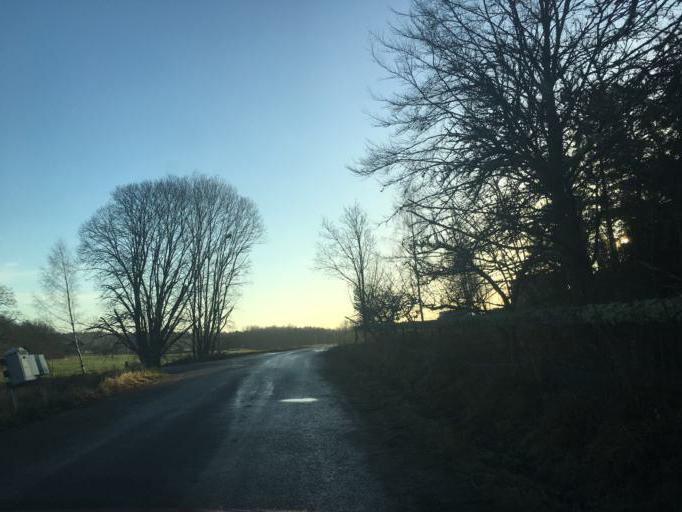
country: SE
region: Kalmar
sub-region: Vasterviks Kommun
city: Ankarsrum
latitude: 57.7092
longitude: 16.4499
